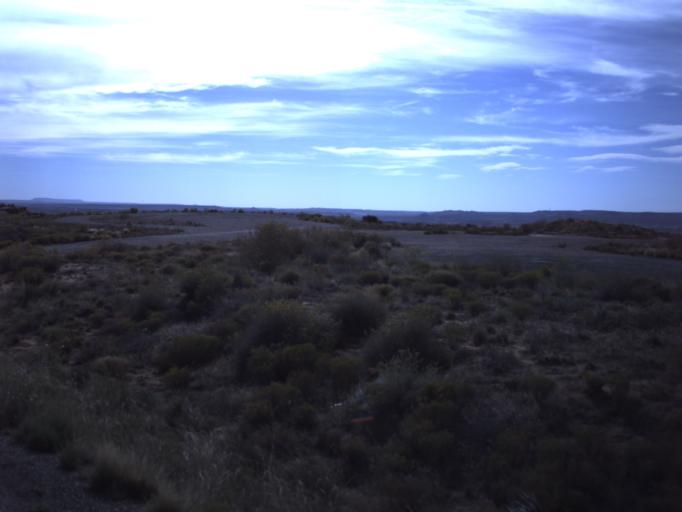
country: US
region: Utah
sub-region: San Juan County
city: Blanding
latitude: 37.3254
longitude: -109.3322
